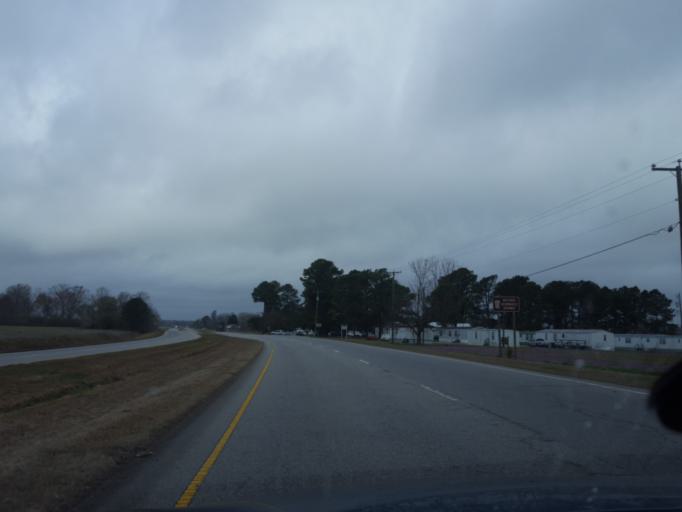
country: US
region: North Carolina
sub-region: Washington County
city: Plymouth
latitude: 35.8315
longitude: -76.7961
